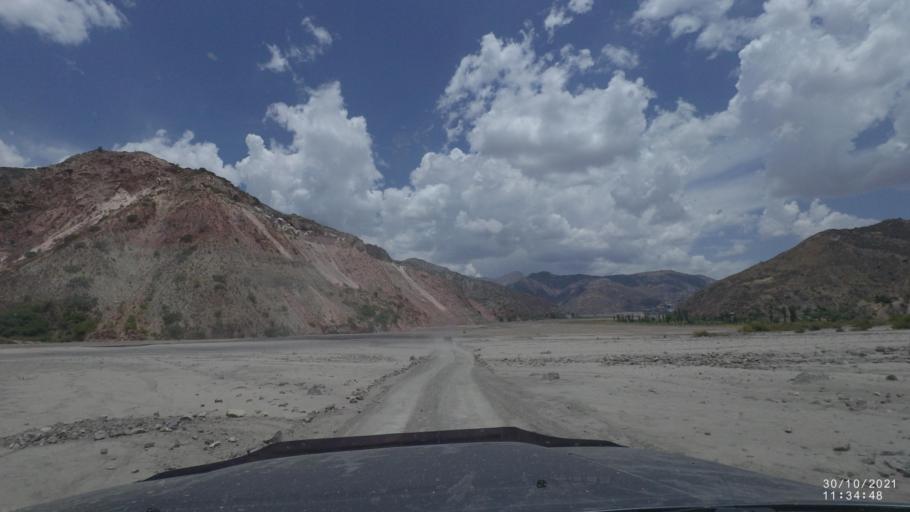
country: BO
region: Cochabamba
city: Sipe Sipe
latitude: -17.5235
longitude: -66.5951
